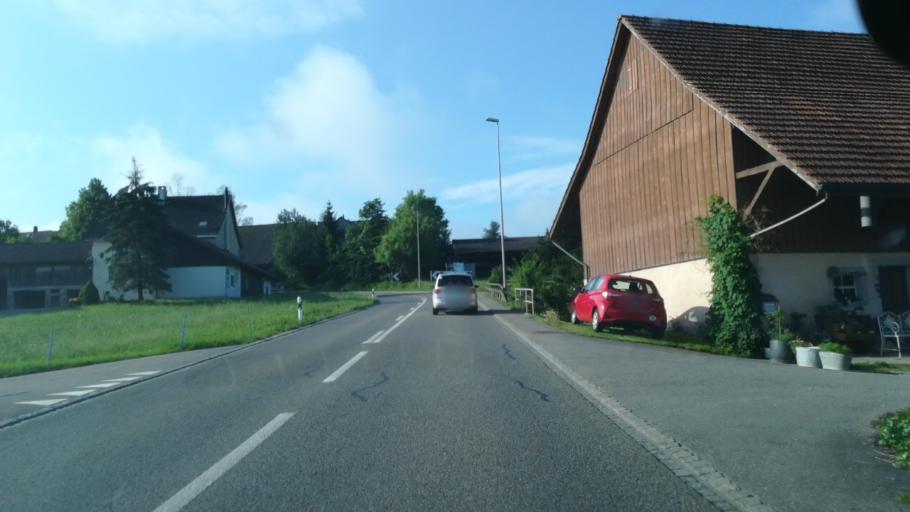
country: CH
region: Thurgau
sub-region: Weinfelden District
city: Sulgen
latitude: 47.5498
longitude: 9.1775
